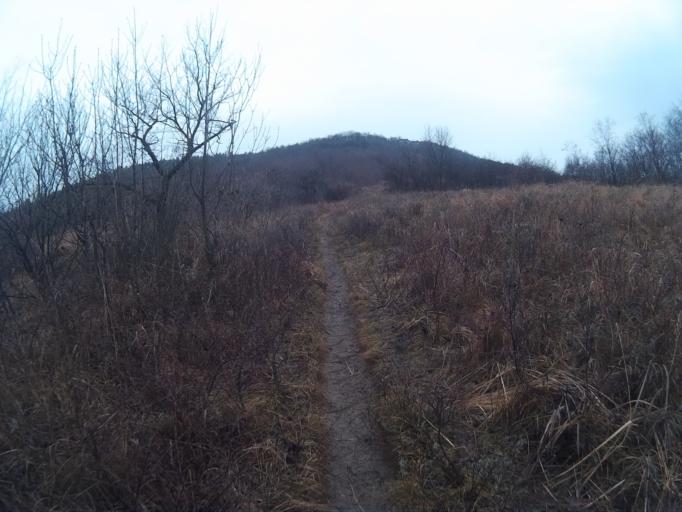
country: HU
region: Komarom-Esztergom
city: Tat
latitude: 47.7213
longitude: 18.6188
